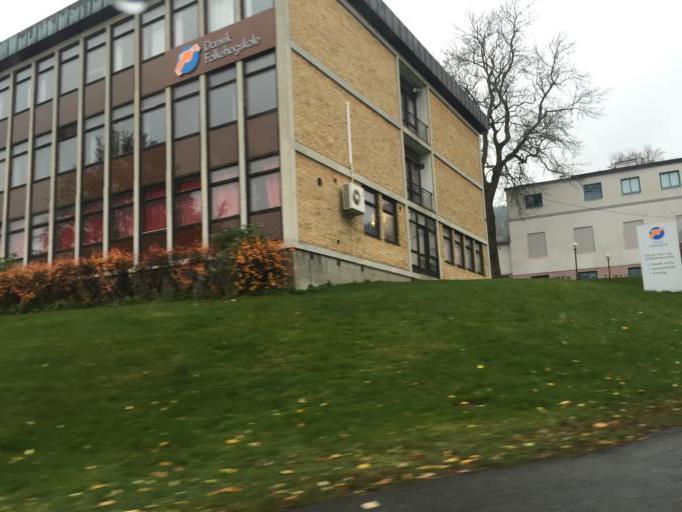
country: NO
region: Buskerud
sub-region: Drammen
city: Drammen
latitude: 59.7332
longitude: 10.1981
